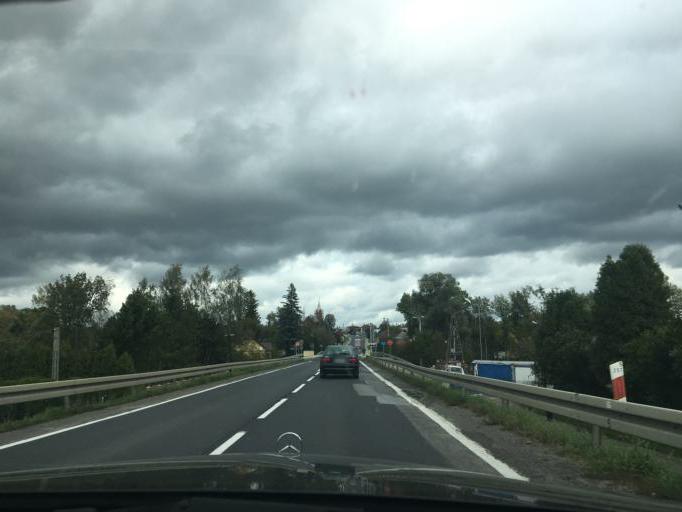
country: PL
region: Subcarpathian Voivodeship
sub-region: Powiat krosnienski
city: Miejsce Piastowe
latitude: 49.6302
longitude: 21.7792
